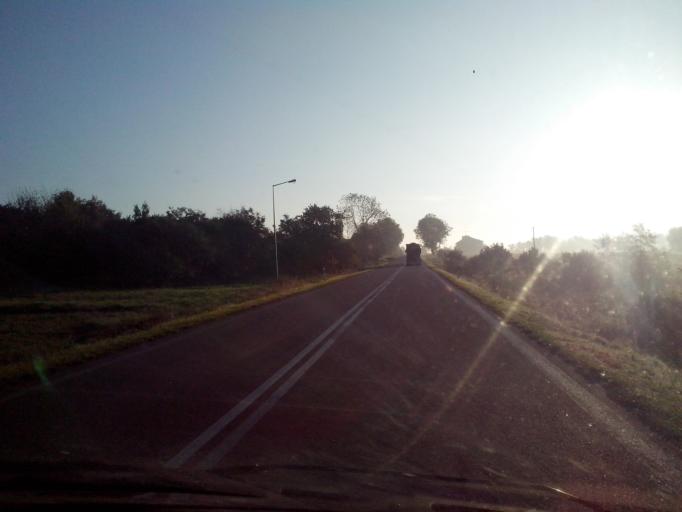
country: PL
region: Subcarpathian Voivodeship
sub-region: Powiat brzozowski
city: Wesola
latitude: 49.8316
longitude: 22.1053
